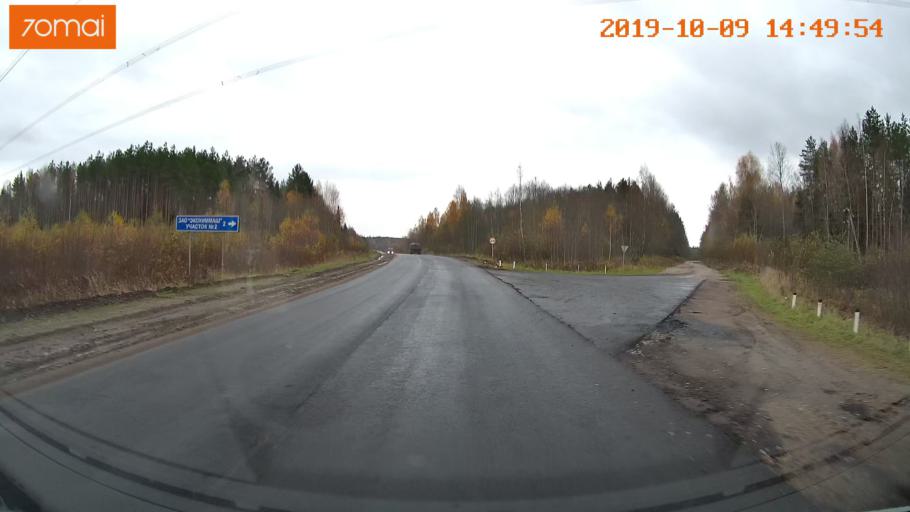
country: RU
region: Kostroma
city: Chistyye Bory
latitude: 58.3887
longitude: 41.5891
